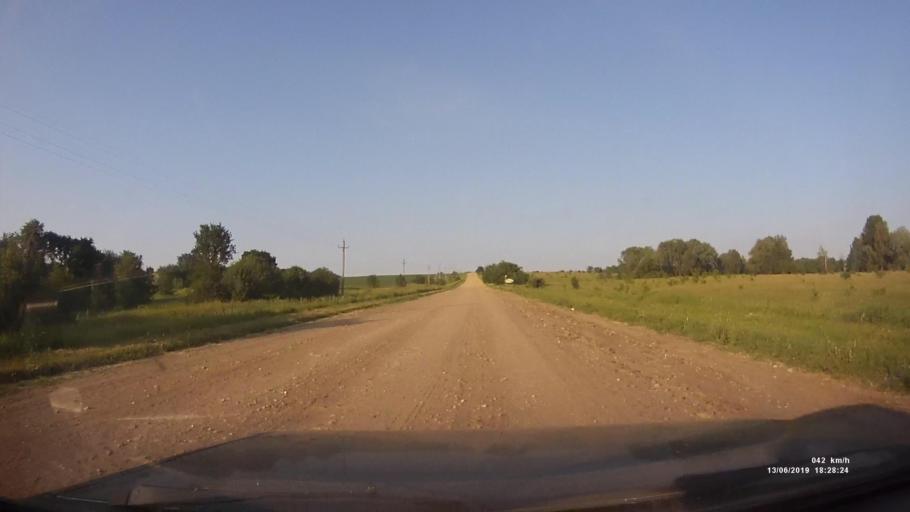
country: RU
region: Rostov
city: Kazanskaya
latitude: 49.8568
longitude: 41.3319
